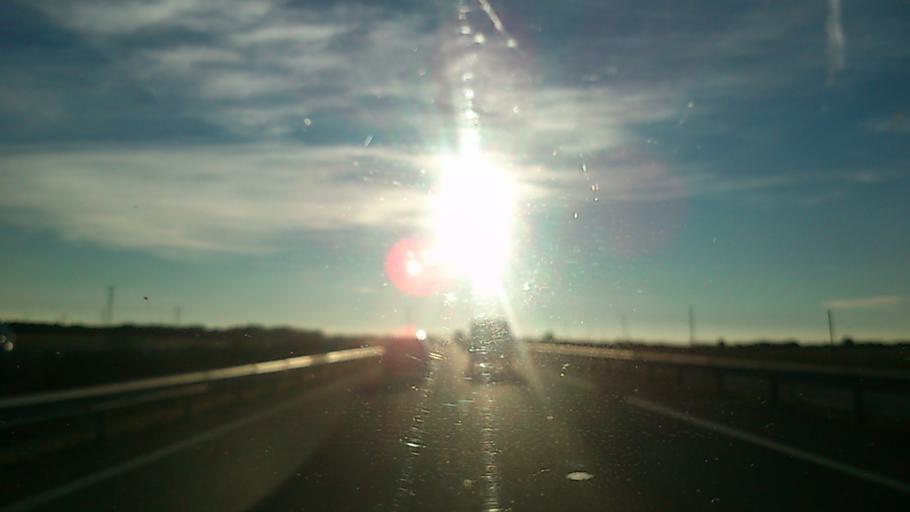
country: ES
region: Castille-La Mancha
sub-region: Provincia de Guadalajara
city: Utande
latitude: 40.8246
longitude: -2.9186
